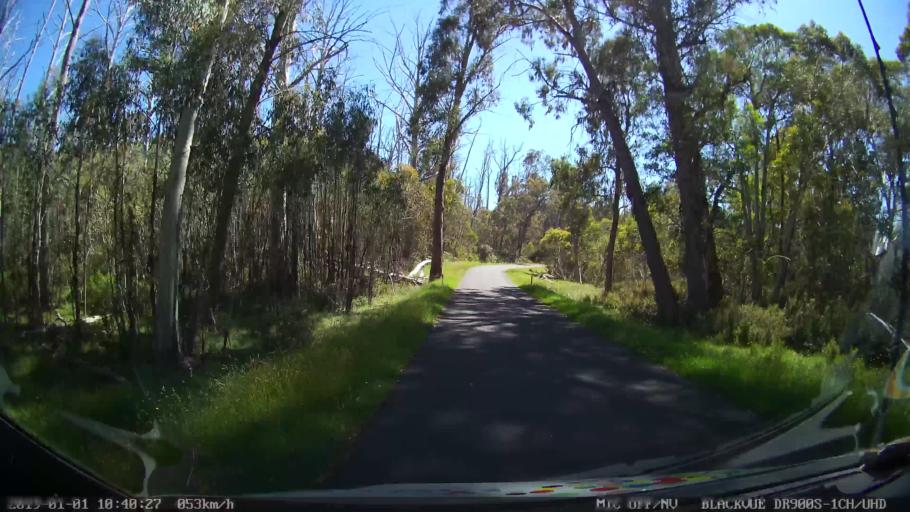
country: AU
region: New South Wales
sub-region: Snowy River
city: Jindabyne
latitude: -36.0381
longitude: 148.3127
